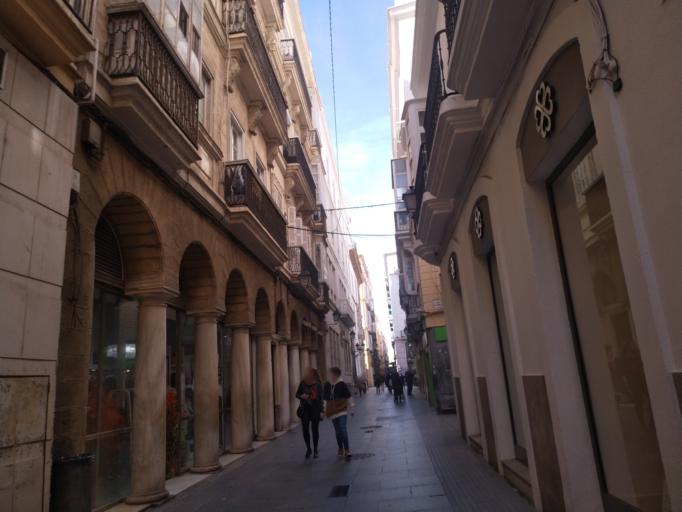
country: ES
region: Andalusia
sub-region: Provincia de Cadiz
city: Cadiz
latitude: 36.5318
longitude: -6.2936
